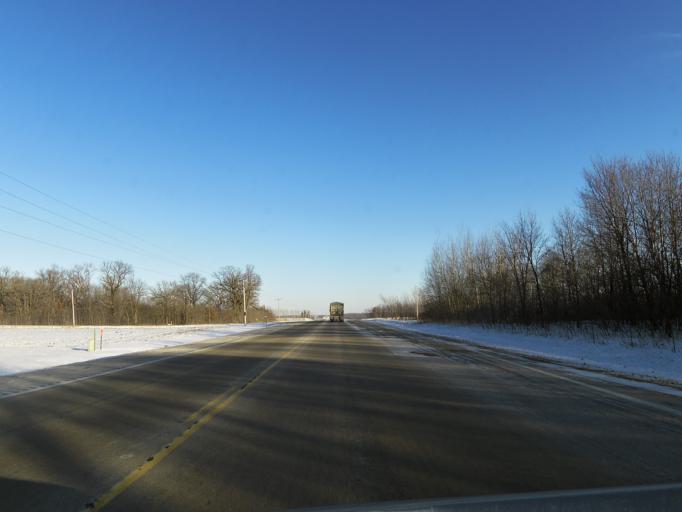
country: US
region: Minnesota
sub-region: Rice County
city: Lonsdale
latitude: 44.4862
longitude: -93.5057
